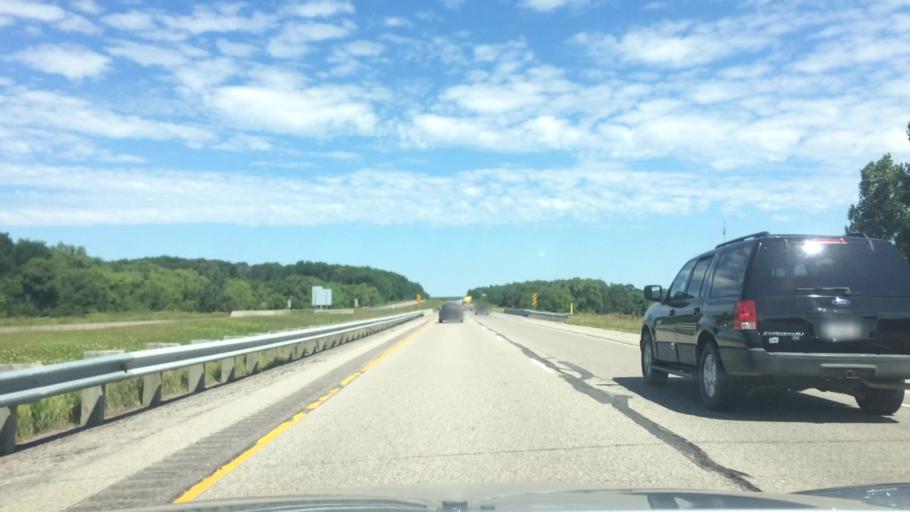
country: US
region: Wisconsin
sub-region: Marquette County
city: Westfield
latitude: 43.7175
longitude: -89.4765
